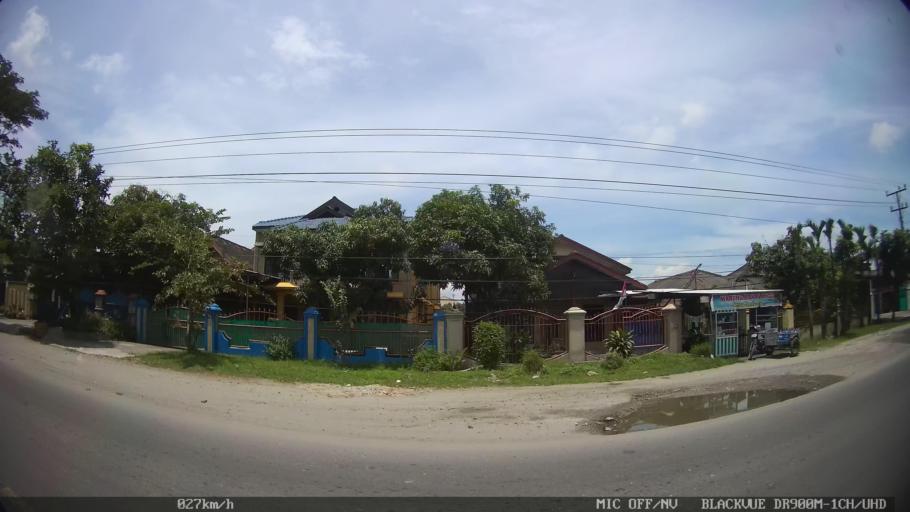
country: ID
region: North Sumatra
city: Labuhan Deli
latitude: 3.7503
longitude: 98.6754
